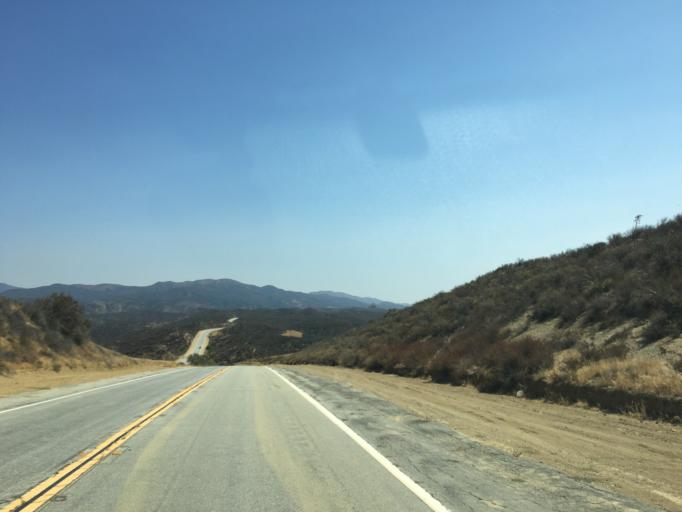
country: US
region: California
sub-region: Los Angeles County
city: Castaic
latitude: 34.5188
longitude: -118.5799
